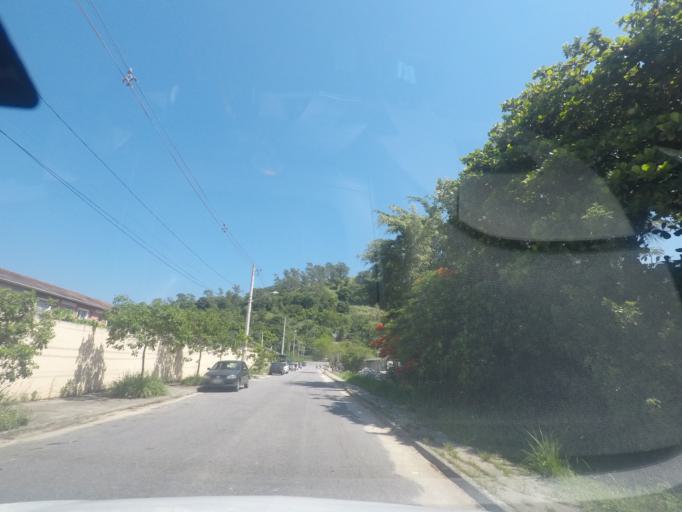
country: BR
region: Rio de Janeiro
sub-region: Nilopolis
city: Nilopolis
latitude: -22.9897
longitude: -43.4848
